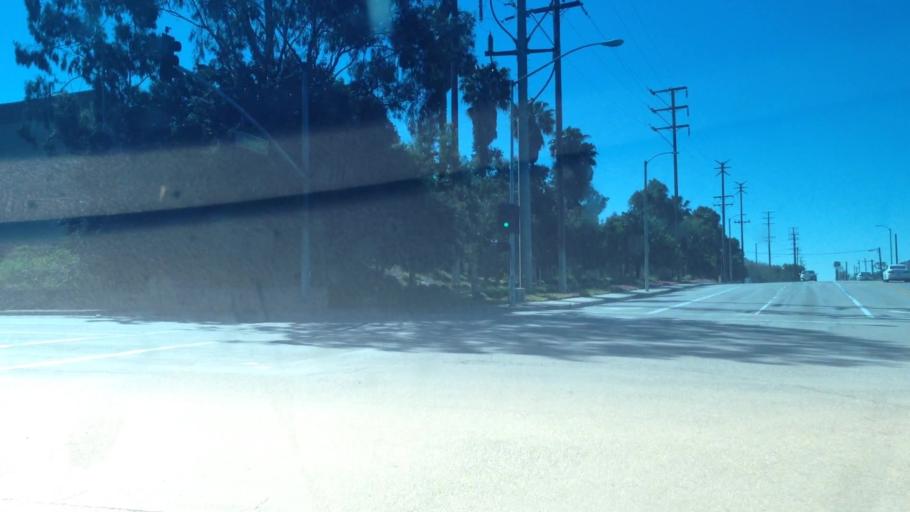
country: US
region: California
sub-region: Los Angeles County
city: Signal Hill
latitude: 33.8118
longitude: -118.1763
